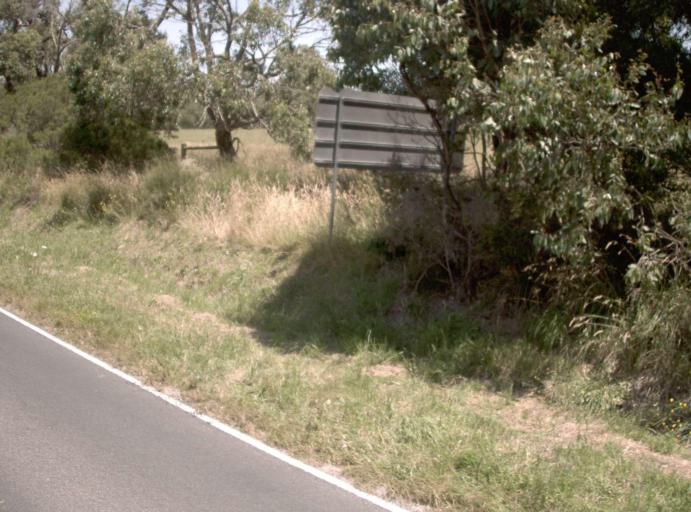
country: AU
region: Victoria
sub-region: Bass Coast
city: North Wonthaggi
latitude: -38.6635
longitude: 145.9285
